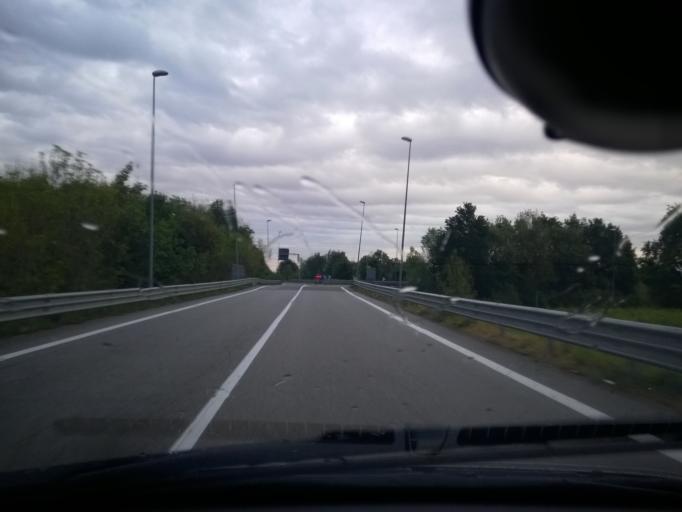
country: IT
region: Veneto
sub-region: Provincia di Venezia
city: Musile di Piave
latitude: 45.5920
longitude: 12.5527
